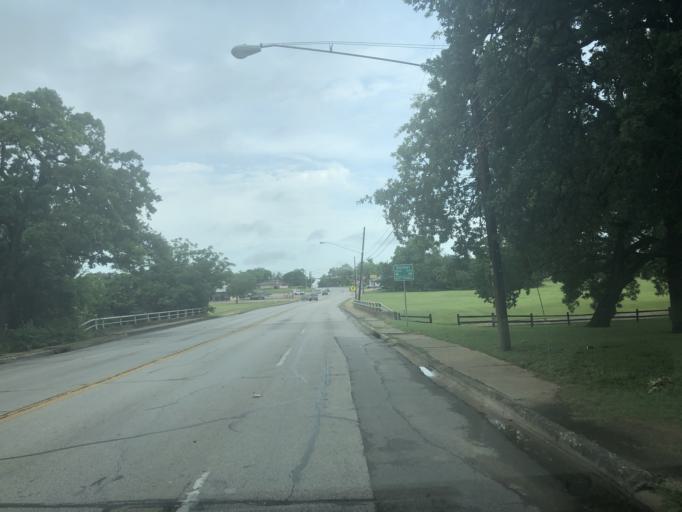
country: US
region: Texas
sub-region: Dallas County
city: Irving
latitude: 32.8011
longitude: -96.9441
